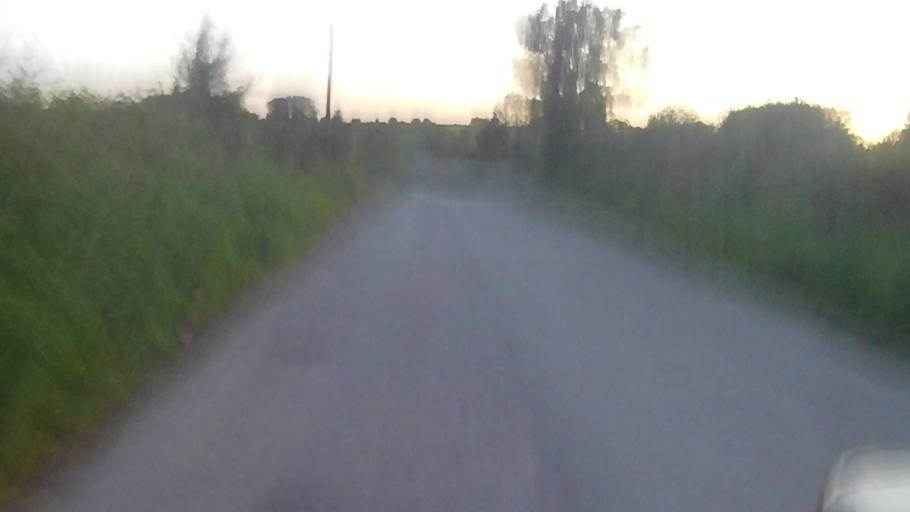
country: IE
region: Munster
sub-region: County Cork
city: Carrigtwohill
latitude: 51.9648
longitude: -8.2872
